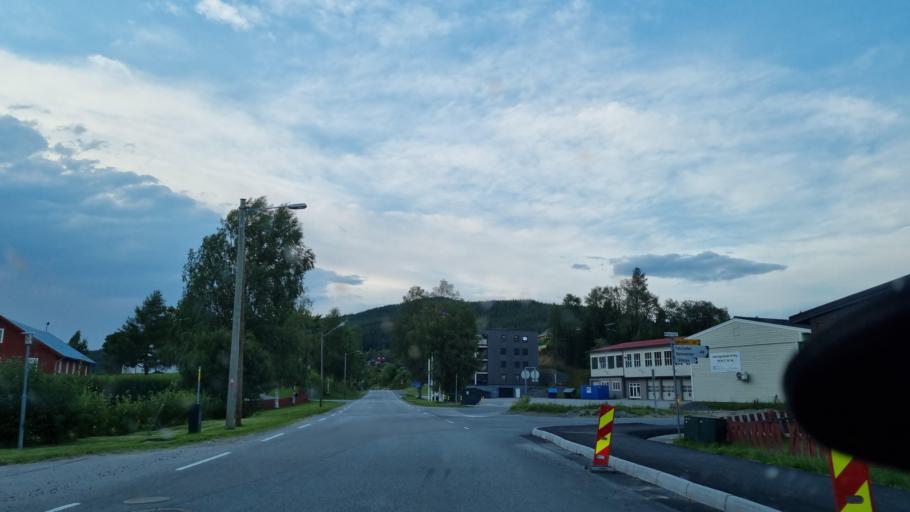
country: NO
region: Hedmark
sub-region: Trysil
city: Innbygda
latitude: 61.3175
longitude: 12.2601
